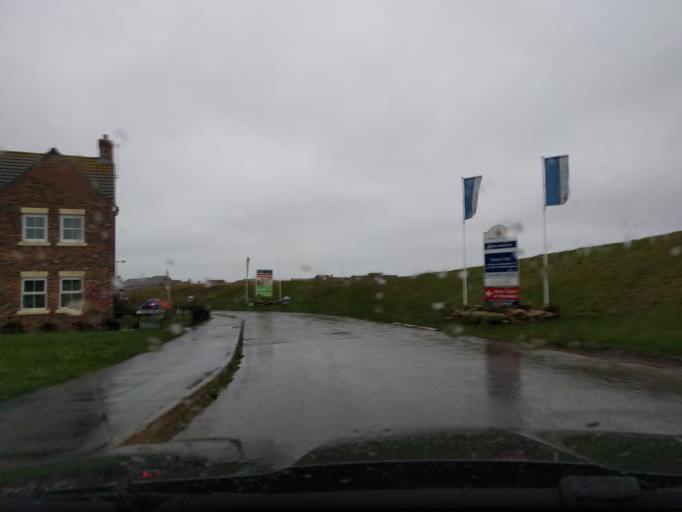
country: GB
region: England
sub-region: Northumberland
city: Lynemouth
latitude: 55.1807
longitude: -1.5489
